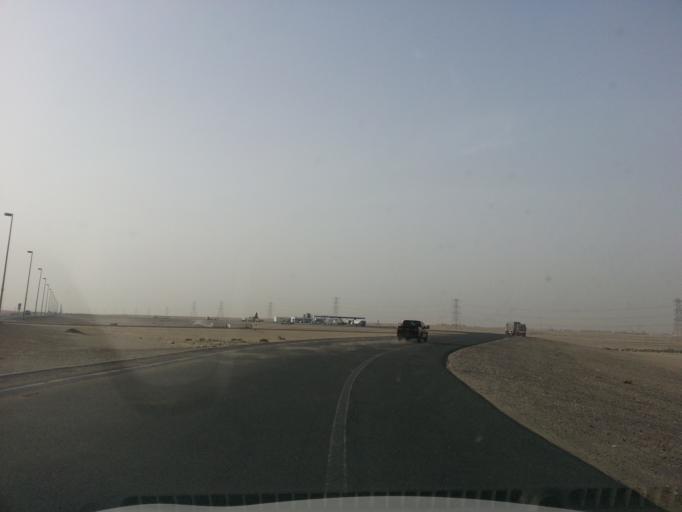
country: AE
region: Dubai
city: Dubai
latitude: 24.8020
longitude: 55.0706
